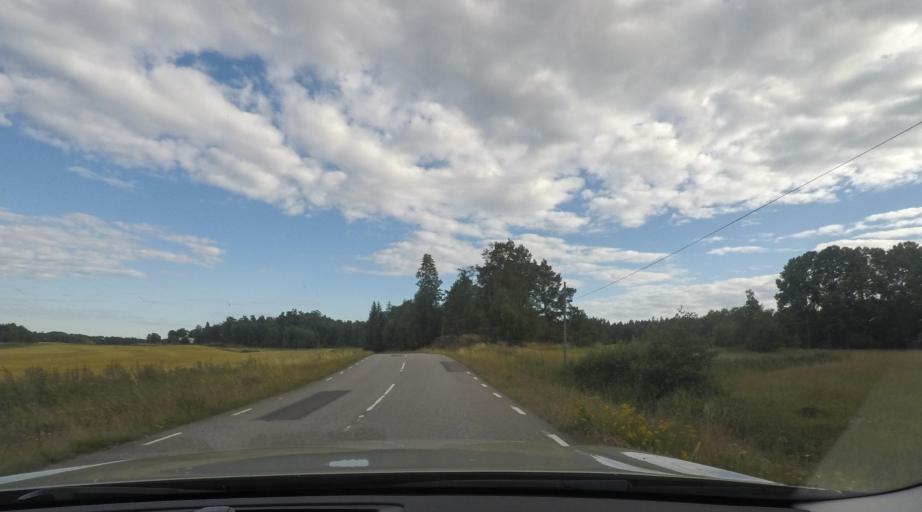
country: SE
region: Soedermanland
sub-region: Trosa Kommun
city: Trosa
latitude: 58.9883
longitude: 17.6773
